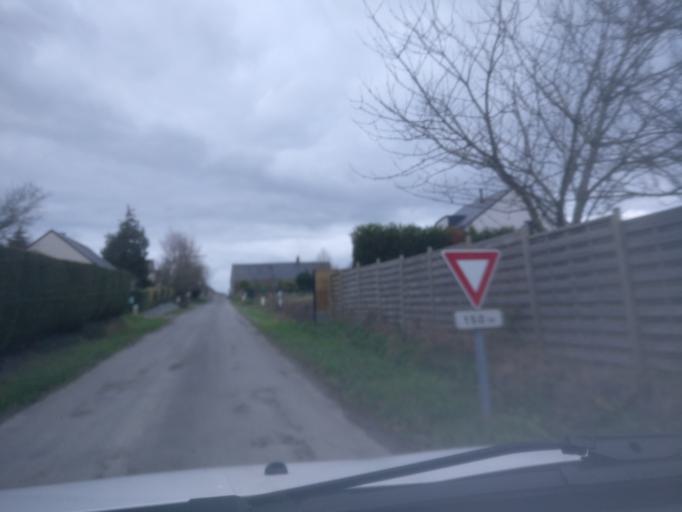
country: FR
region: Lower Normandy
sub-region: Departement de la Manche
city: Marcey-les-Greves
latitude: 48.6733
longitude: -1.4093
